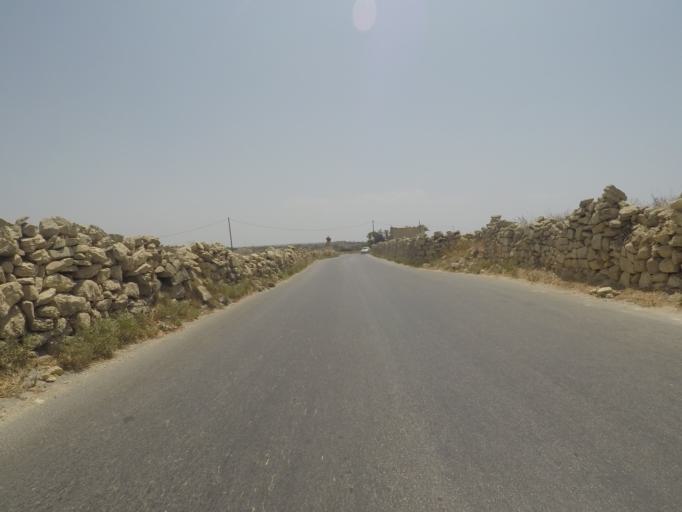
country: MT
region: Is-Siggiewi
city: Siggiewi
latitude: 35.8528
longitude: 14.4303
